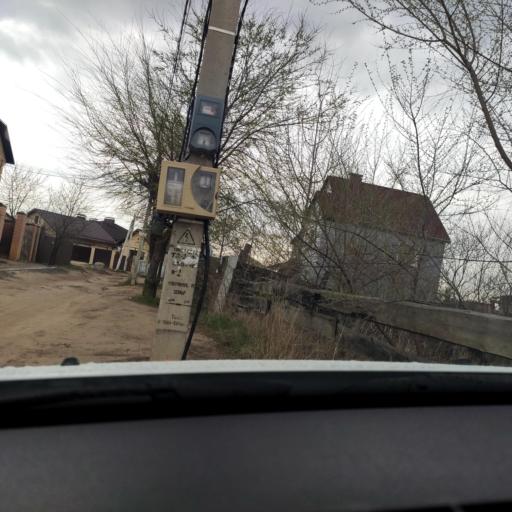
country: RU
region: Voronezj
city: Podgornoye
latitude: 51.7473
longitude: 39.1454
